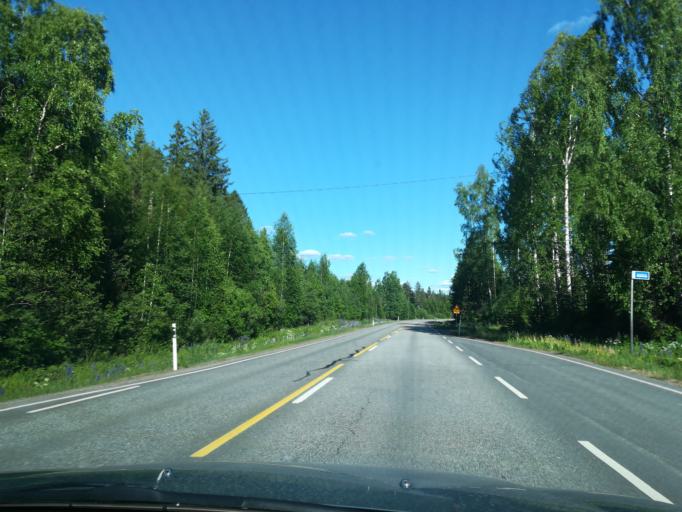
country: FI
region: South Karelia
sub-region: Imatra
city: Ruokolahti
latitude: 61.3527
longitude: 28.7284
